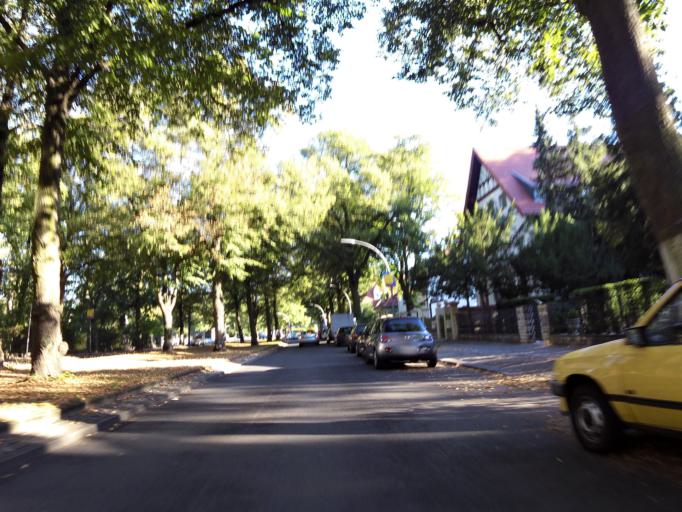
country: DE
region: Berlin
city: Dahlem
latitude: 52.4600
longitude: 13.3020
